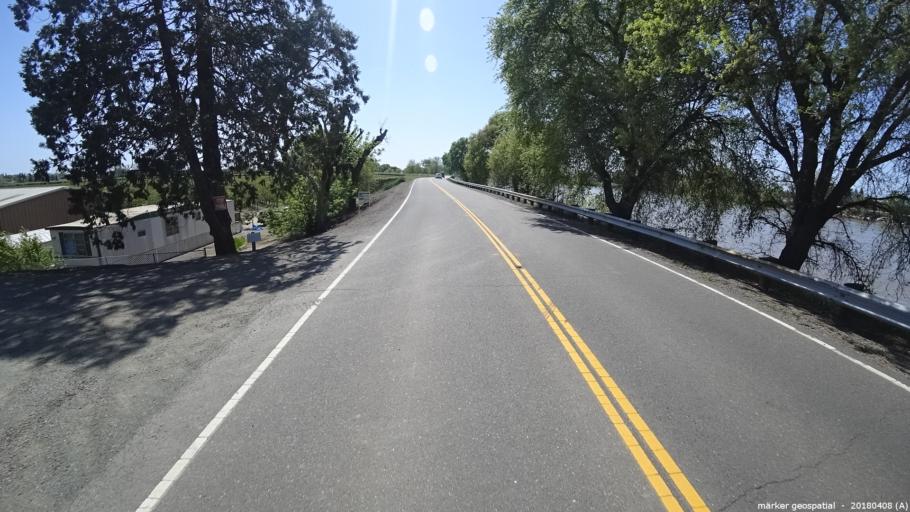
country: US
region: California
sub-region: Sacramento County
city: Laguna
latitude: 38.3819
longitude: -121.5197
